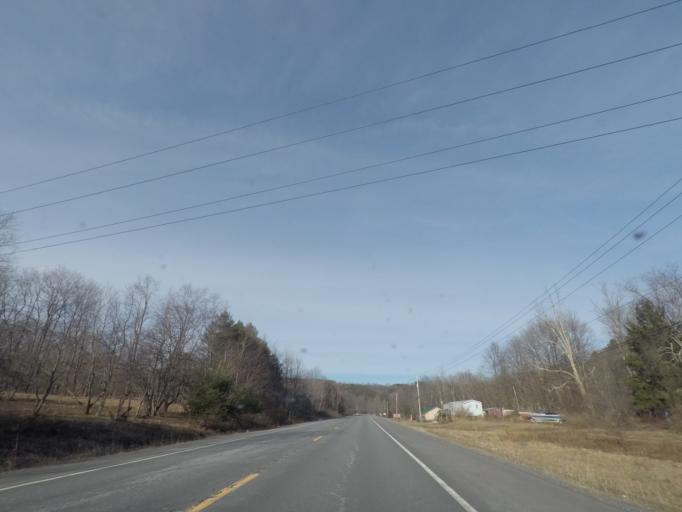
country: US
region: Massachusetts
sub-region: Berkshire County
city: Williamstown
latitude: 42.7359
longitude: -73.3611
